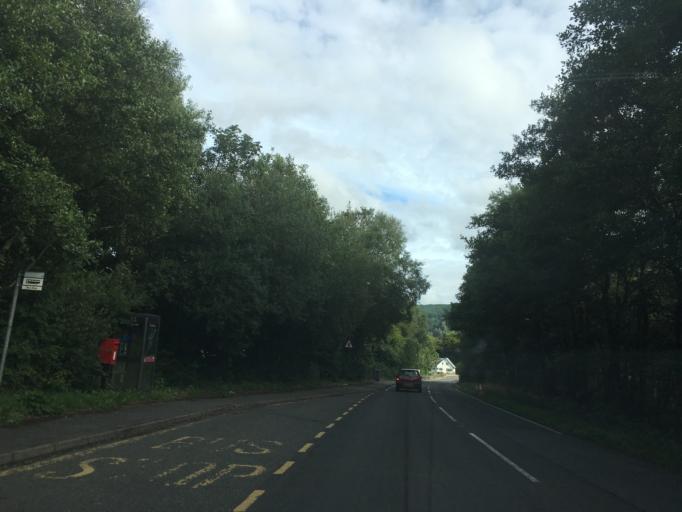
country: GB
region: Scotland
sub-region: Argyll and Bute
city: Oban
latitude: 56.3744
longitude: -5.4411
